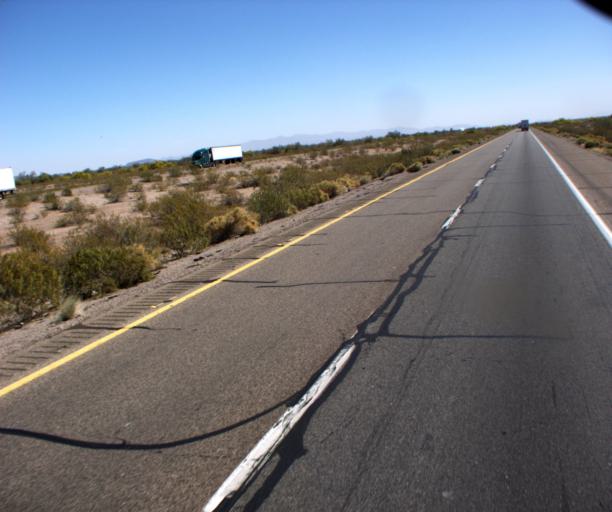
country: US
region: Arizona
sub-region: Maricopa County
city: Buckeye
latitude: 33.5094
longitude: -113.0057
